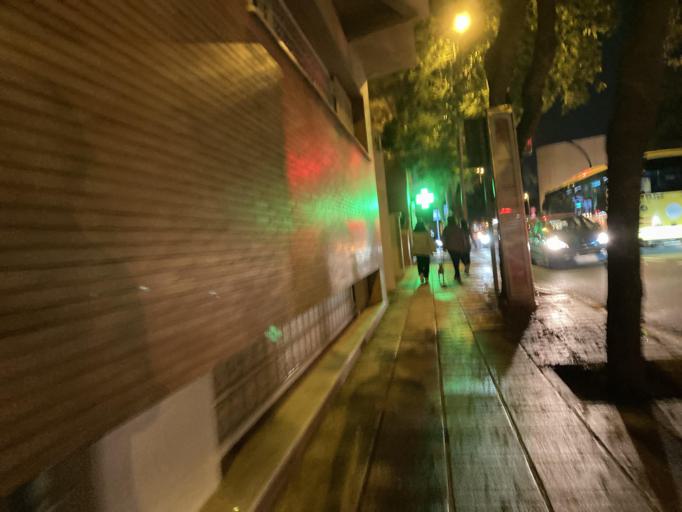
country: ES
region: Murcia
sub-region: Murcia
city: Murcia
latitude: 37.9999
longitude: -1.1263
